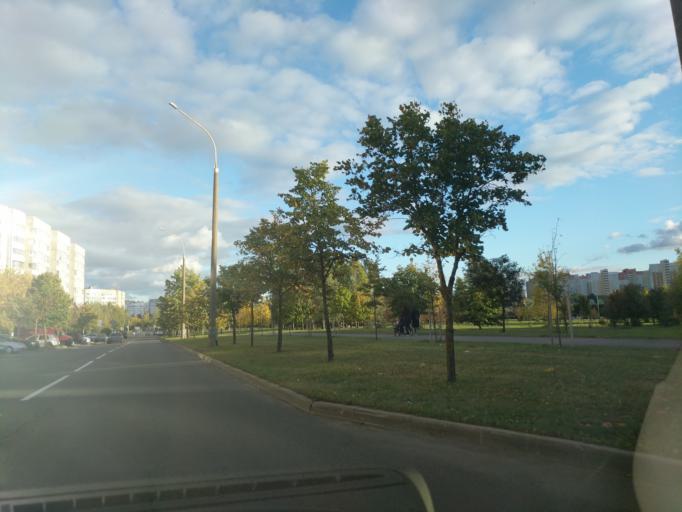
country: BY
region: Minsk
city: Malinovka
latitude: 53.8588
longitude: 27.4530
